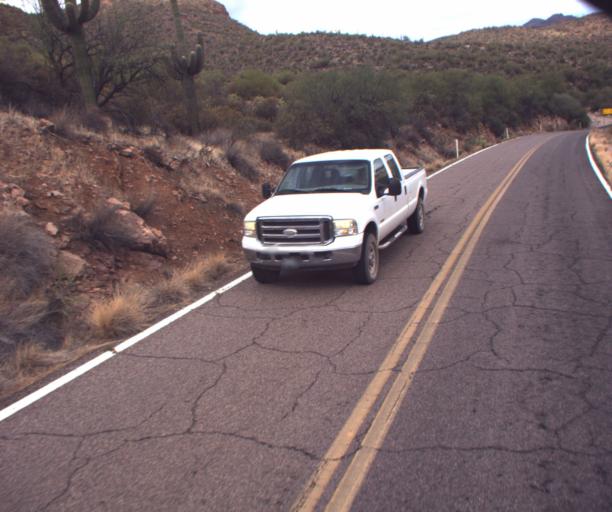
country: US
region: Arizona
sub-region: Pinal County
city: Apache Junction
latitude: 33.5339
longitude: -111.3786
